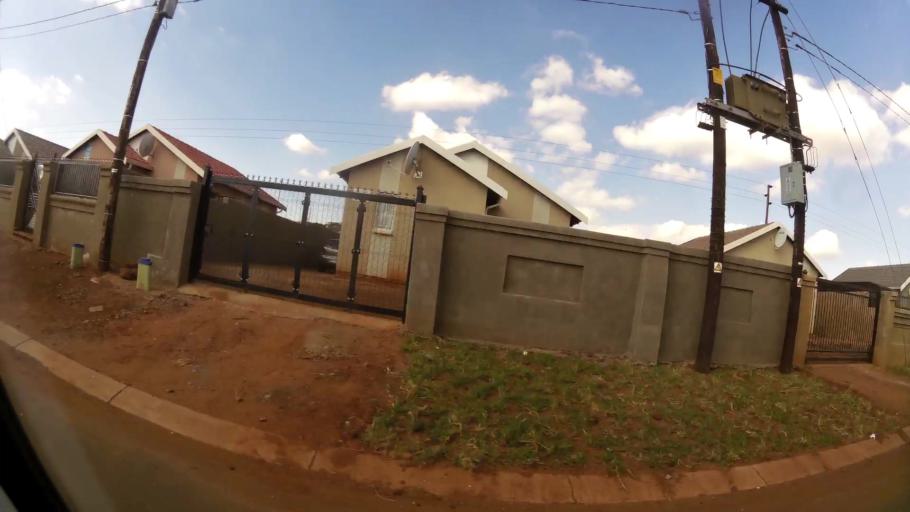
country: ZA
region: Gauteng
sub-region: City of Tshwane Metropolitan Municipality
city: Cullinan
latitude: -25.6897
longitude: 28.4085
